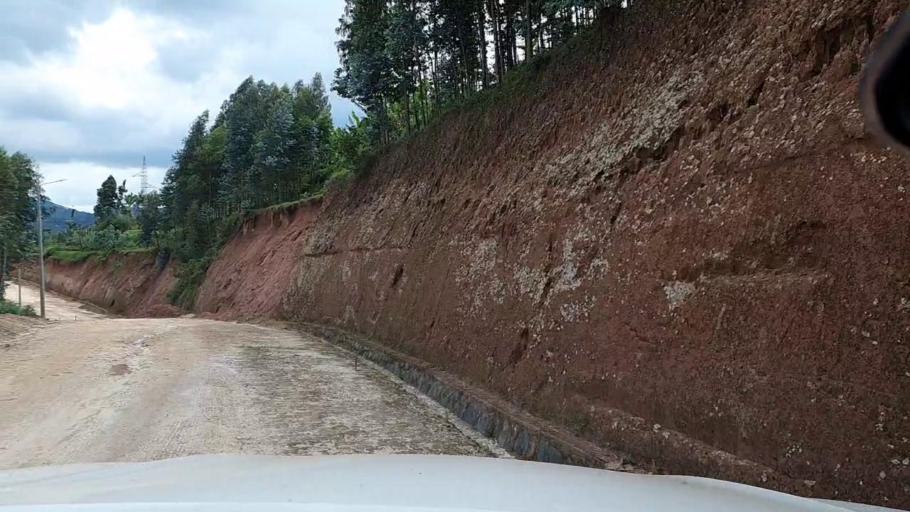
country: RW
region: Southern Province
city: Nzega
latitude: -2.6904
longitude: 29.4435
